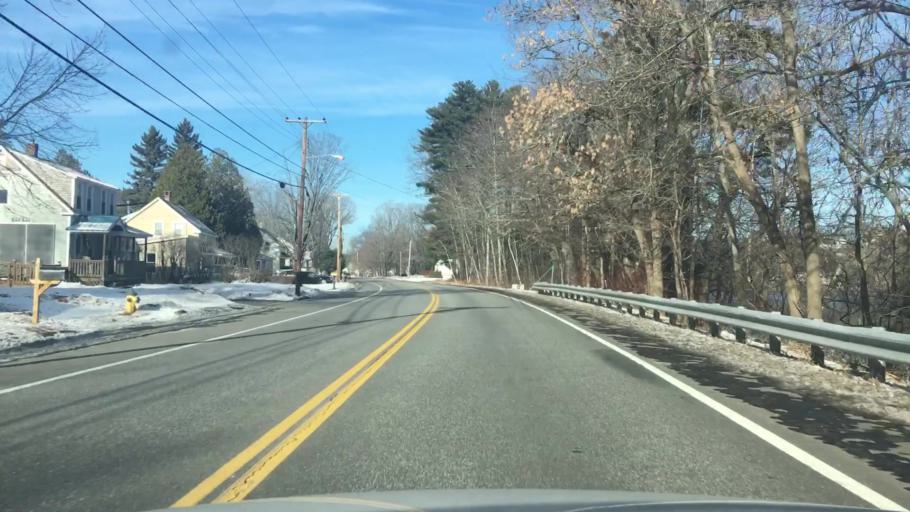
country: US
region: Maine
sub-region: Androscoggin County
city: Lewiston
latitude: 44.0723
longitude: -70.2090
